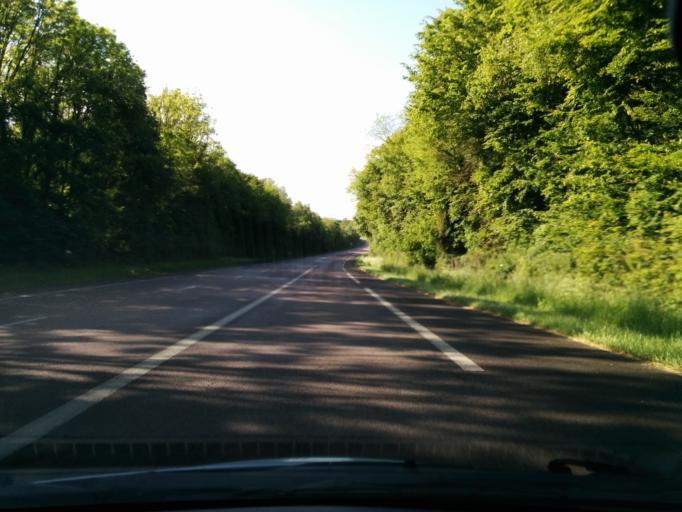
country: FR
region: Ile-de-France
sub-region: Departement des Yvelines
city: Bonnieres-sur-Seine
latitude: 49.0232
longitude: 1.5863
